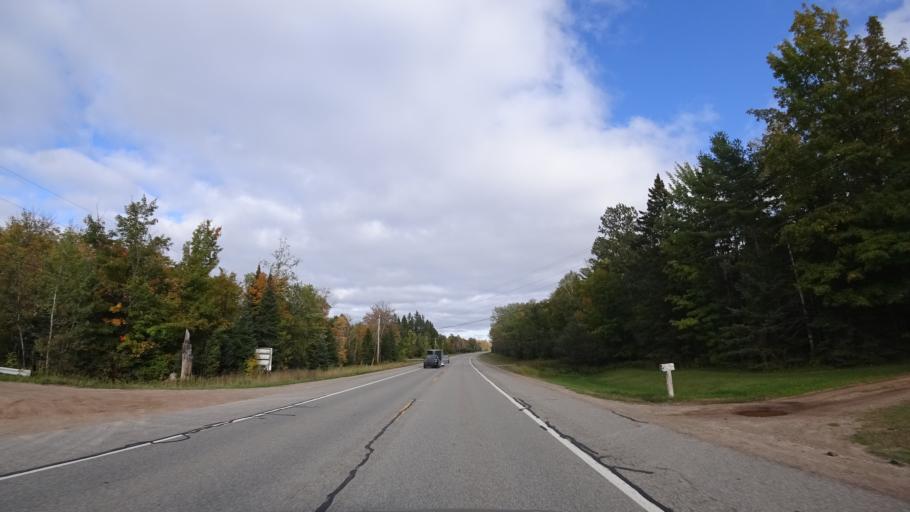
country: US
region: Michigan
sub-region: Alger County
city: Munising
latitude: 46.4420
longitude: -86.7429
